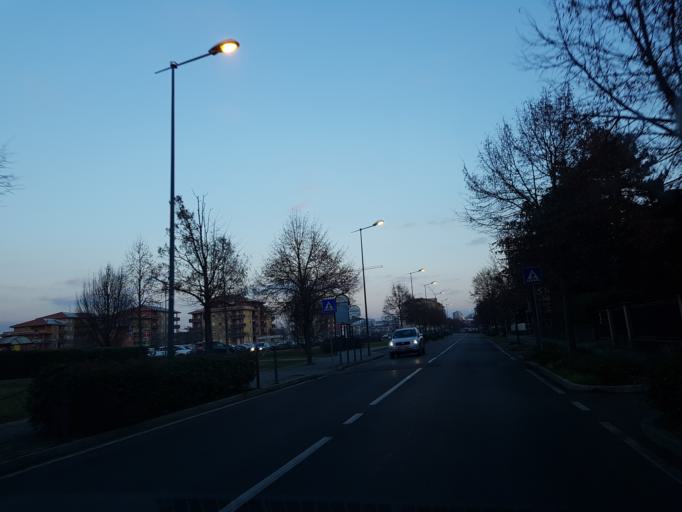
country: IT
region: Piedmont
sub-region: Provincia di Alessandria
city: Novi Ligure
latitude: 44.7656
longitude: 8.7718
